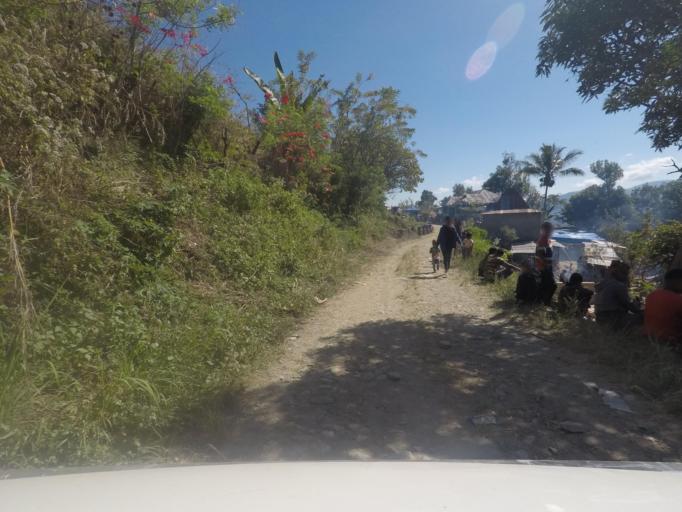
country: TL
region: Ermera
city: Gleno
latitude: -8.7238
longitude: 125.3322
